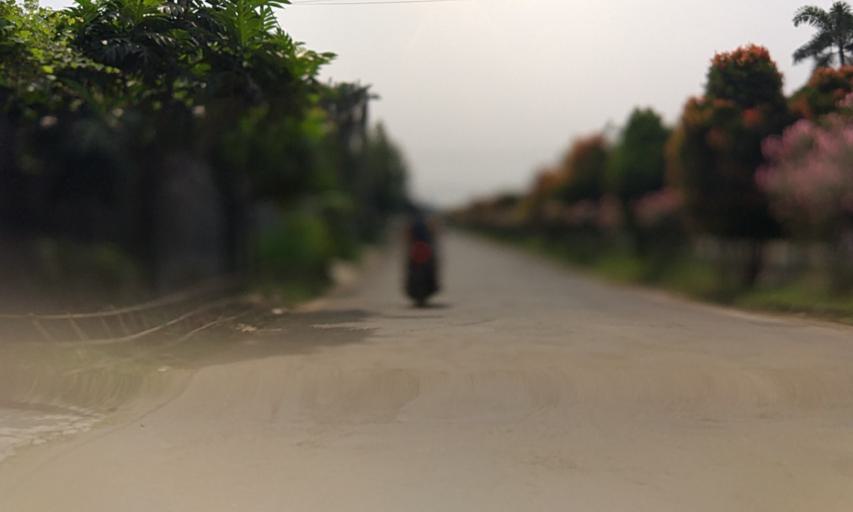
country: ID
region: West Java
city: Margahayukencana
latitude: -6.9448
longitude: 107.5622
